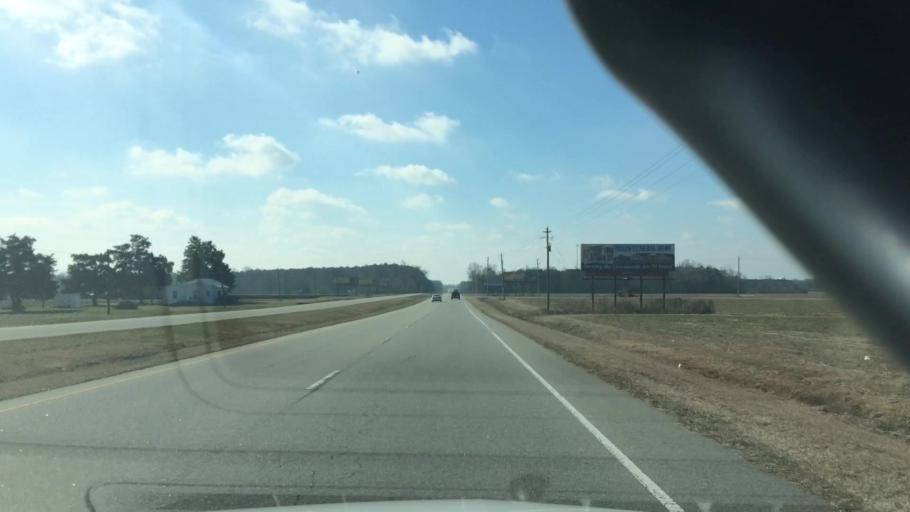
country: US
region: North Carolina
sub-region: Pitt County
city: Grifton
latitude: 35.3474
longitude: -77.4708
